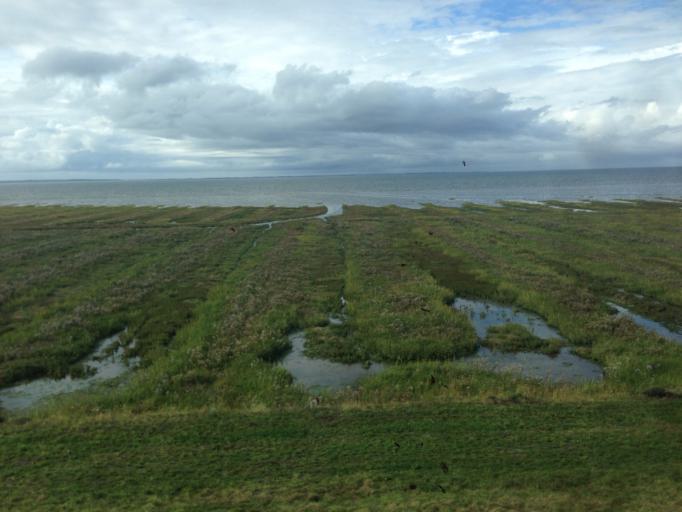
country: DE
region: Schleswig-Holstein
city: Sylt-Ost
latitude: 54.8805
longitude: 8.5015
